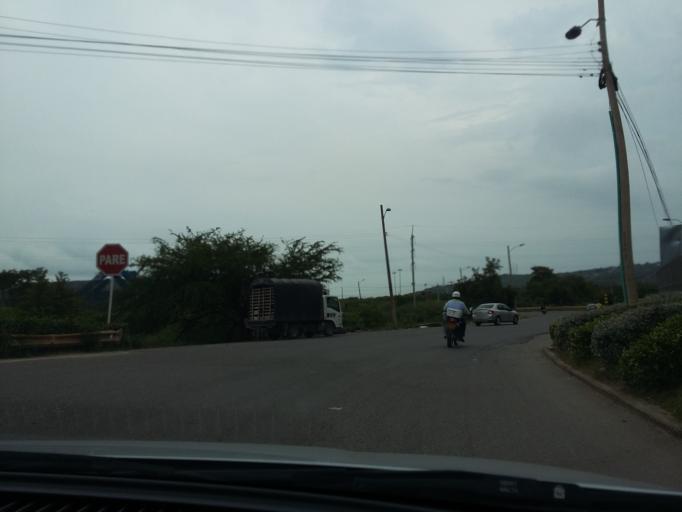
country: CO
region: Bolivar
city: Cartagena
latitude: 10.3429
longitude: -75.4948
